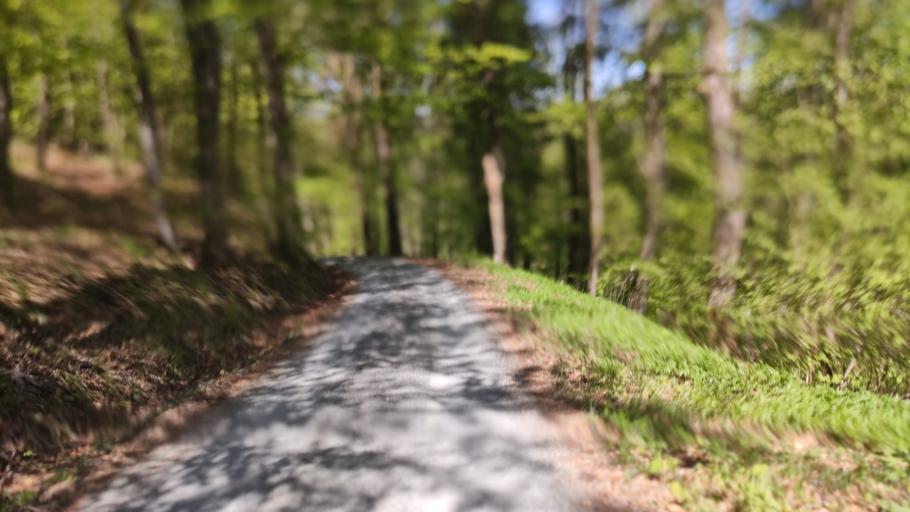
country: DE
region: Bavaria
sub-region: Upper Franconia
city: Nordhalben
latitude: 50.3580
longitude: 11.4784
